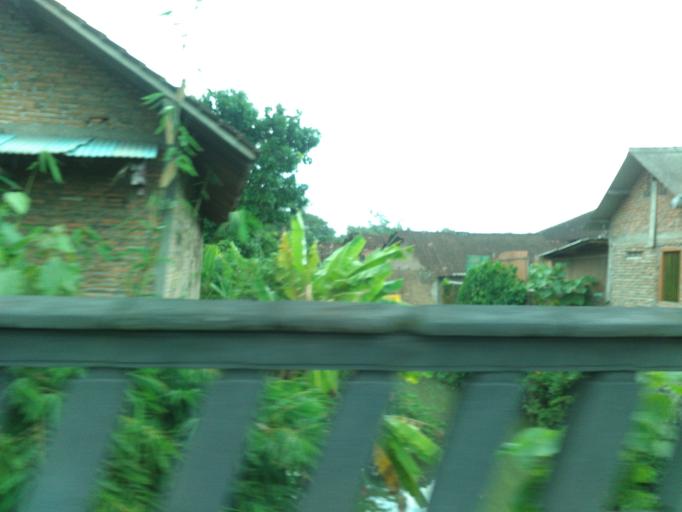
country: ID
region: Central Java
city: Ceper
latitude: -7.6525
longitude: 110.6824
